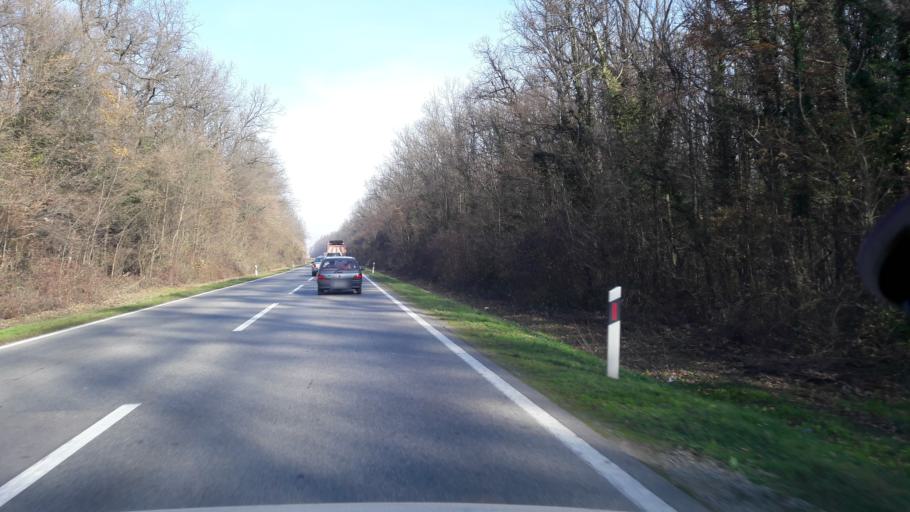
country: HR
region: Vukovarsko-Srijemska
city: Gradiste
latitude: 45.1218
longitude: 18.7110
